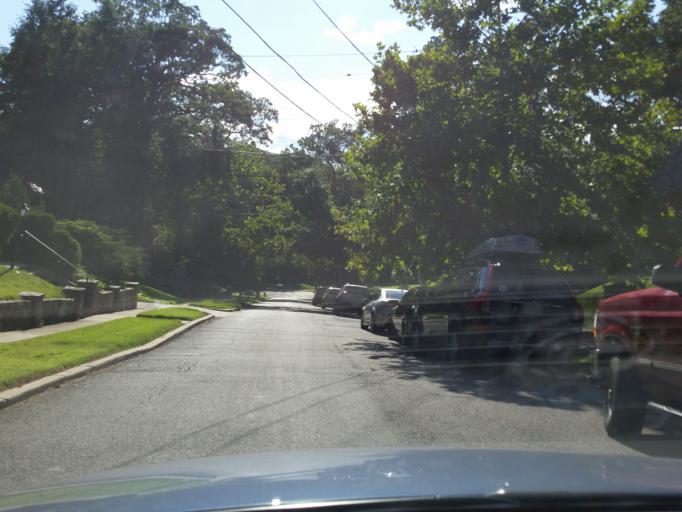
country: US
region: Maryland
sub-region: Montgomery County
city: Silver Spring
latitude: 38.9833
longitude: -77.0368
